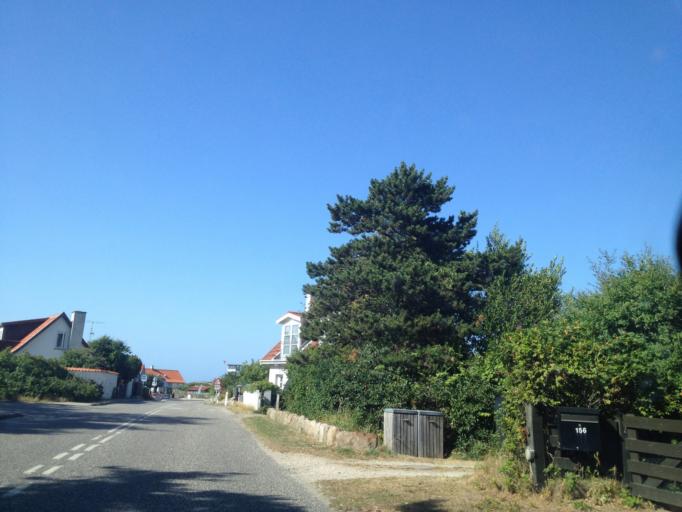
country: DK
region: Capital Region
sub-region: Gribskov Kommune
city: Helsinge
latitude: 56.0966
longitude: 12.1591
